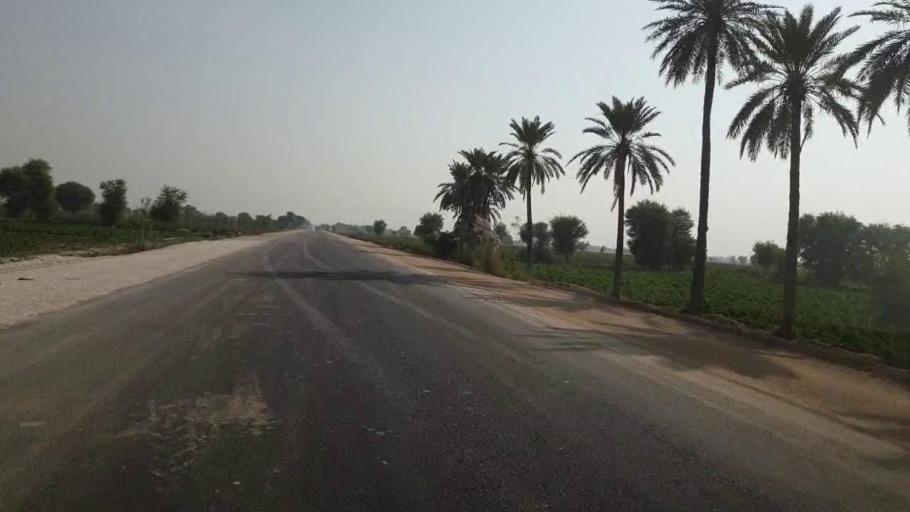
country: PK
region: Sindh
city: Bhan
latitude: 26.5457
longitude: 67.7869
